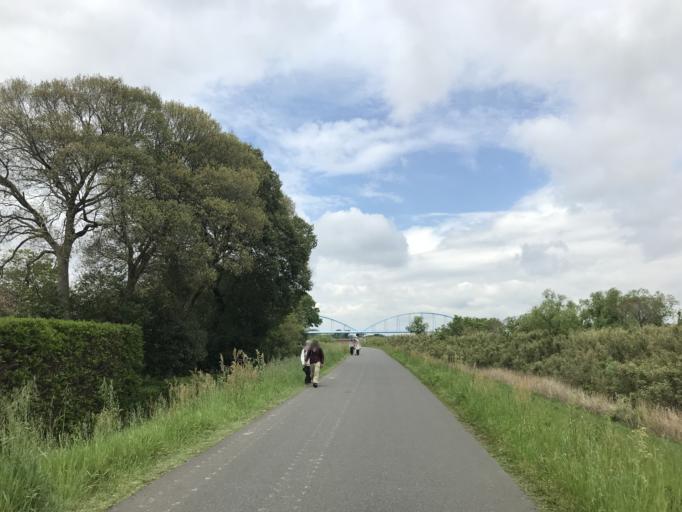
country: JP
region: Ibaraki
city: Mitsukaido
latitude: 35.9865
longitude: 139.9910
